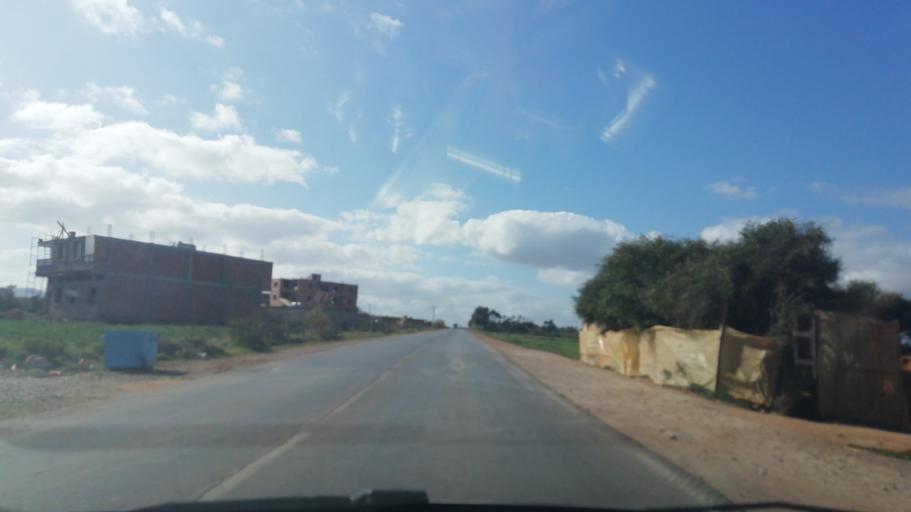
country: DZ
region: Relizane
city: Mazouna
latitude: 36.3284
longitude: 0.6880
